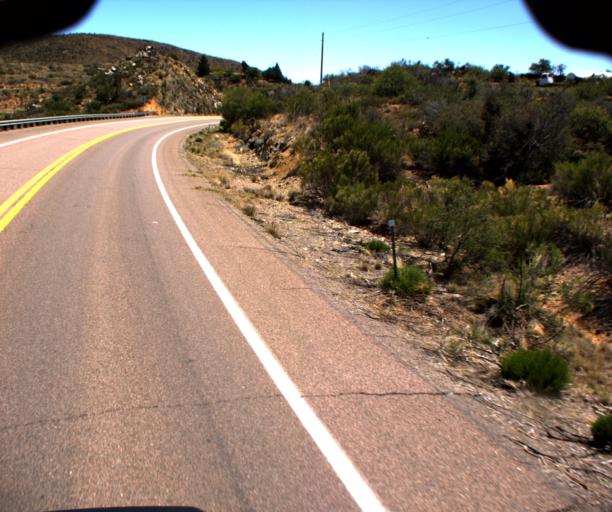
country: US
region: Arizona
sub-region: Yavapai County
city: Bagdad
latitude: 34.5650
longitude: -113.1710
